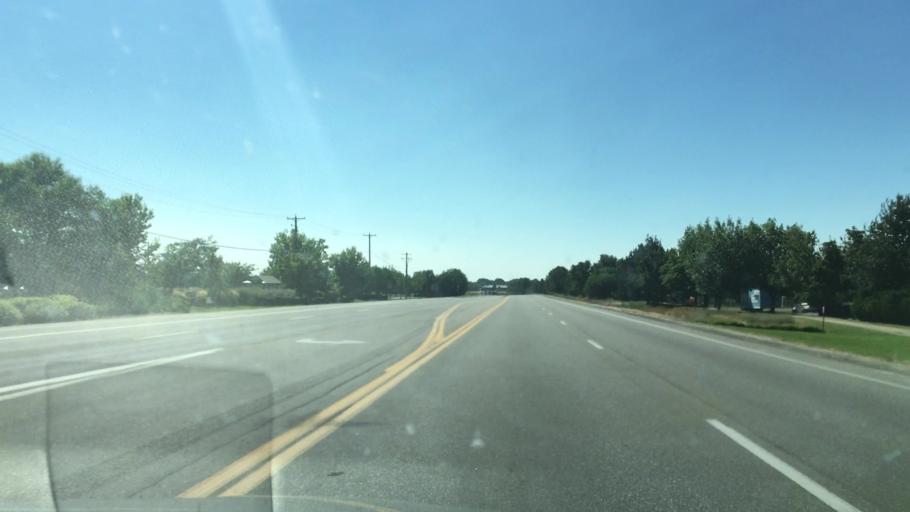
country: US
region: Idaho
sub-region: Ada County
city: Eagle
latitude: 43.6881
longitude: -116.3348
